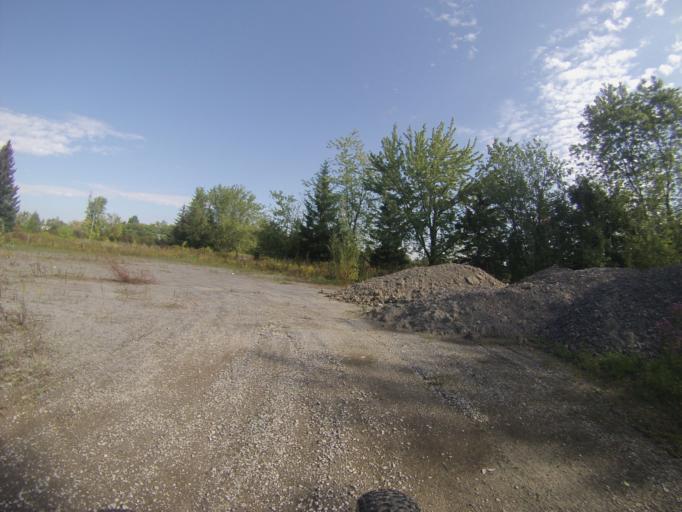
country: CA
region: Ontario
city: Ottawa
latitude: 45.3766
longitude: -75.6224
